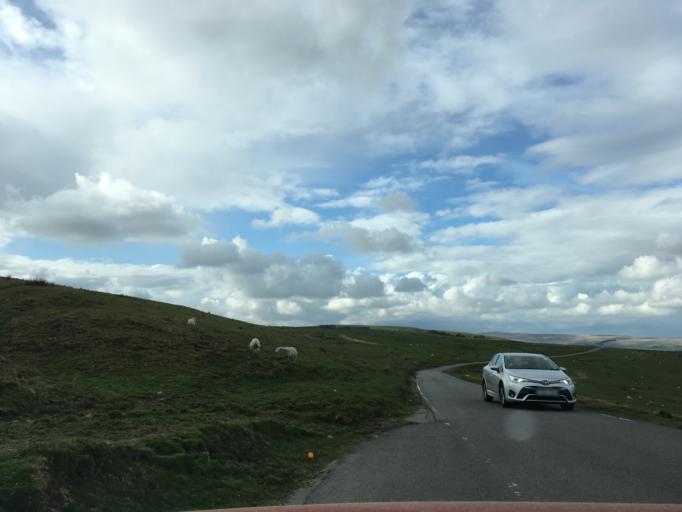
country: GB
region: Wales
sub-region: Caerphilly County Borough
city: Rhymney
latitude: 51.7224
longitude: -3.2970
